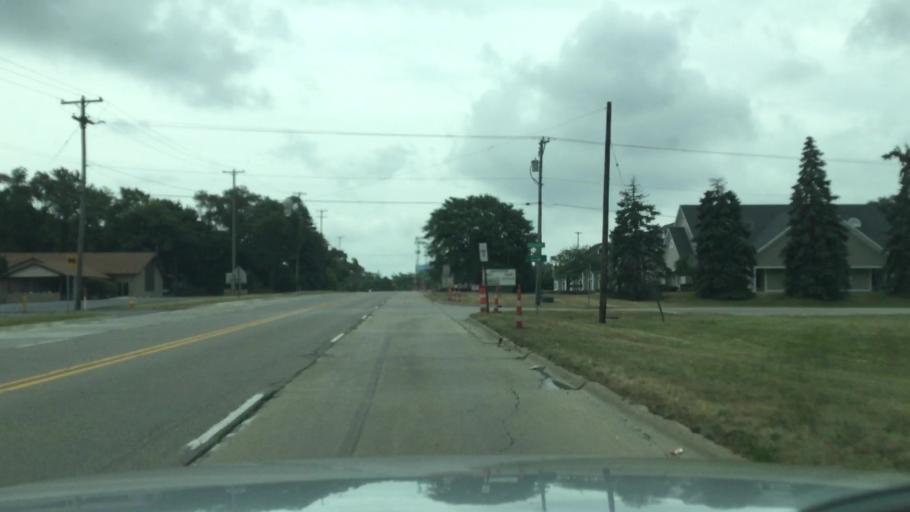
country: US
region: Michigan
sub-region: Genesee County
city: Flint
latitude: 43.0193
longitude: -83.7528
